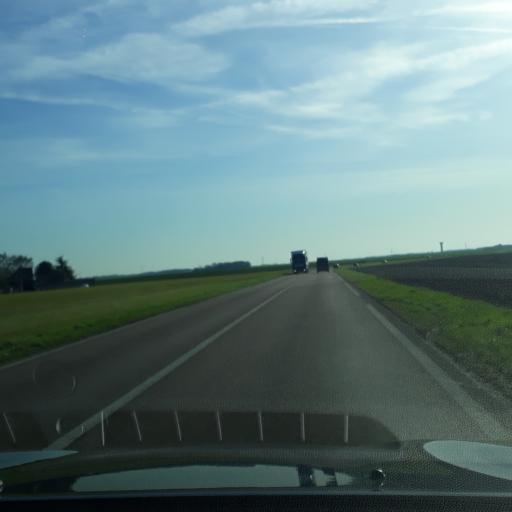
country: FR
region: Ile-de-France
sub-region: Departement de l'Essonne
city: Corbreuse
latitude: 48.4497
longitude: 1.9616
